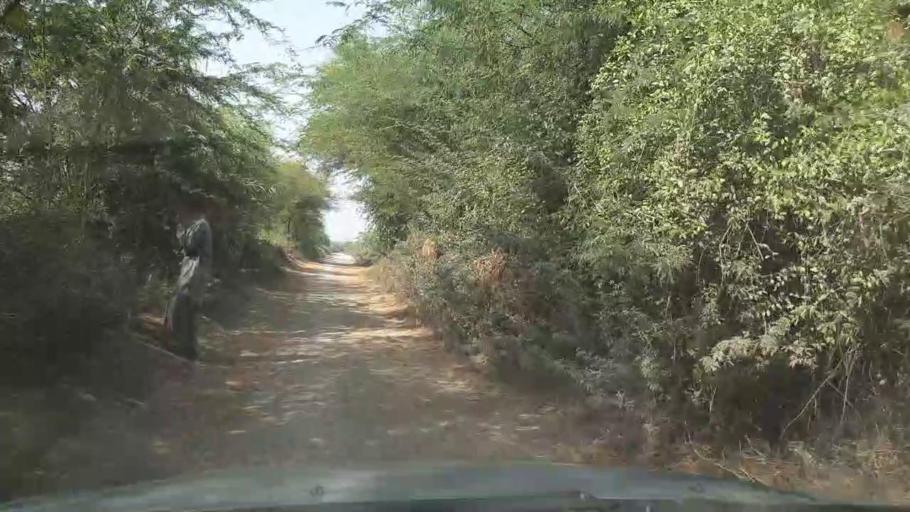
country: PK
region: Sindh
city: Bulri
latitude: 24.8731
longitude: 68.3156
